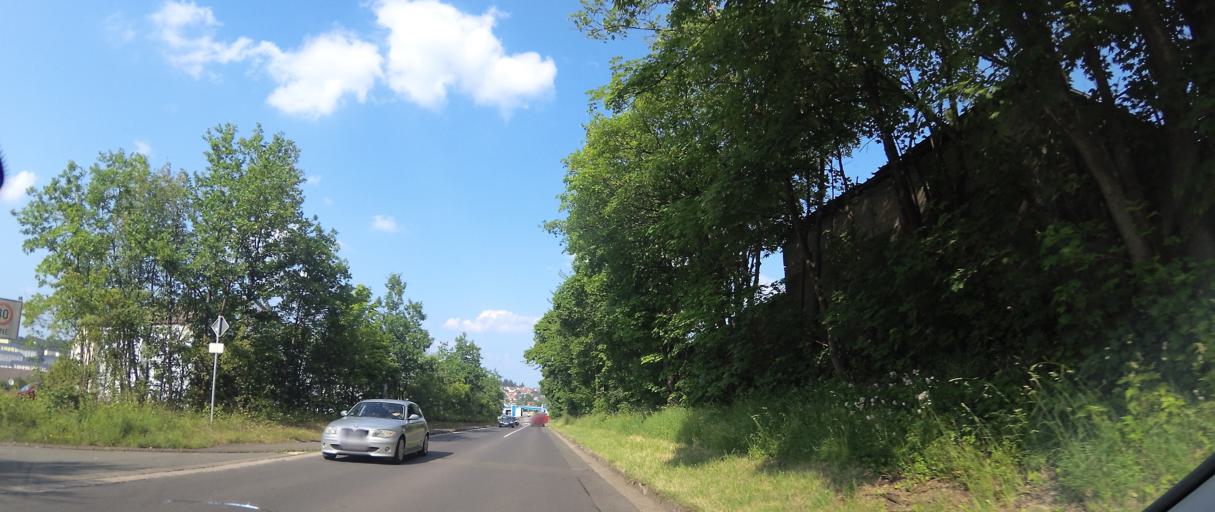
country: DE
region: Rheinland-Pfalz
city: Baumholder
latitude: 49.6083
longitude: 7.3264
